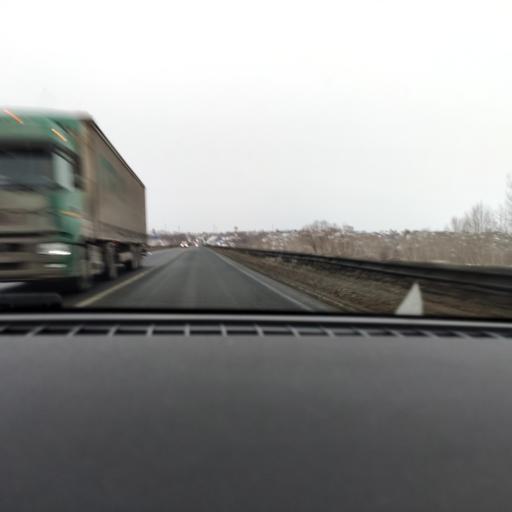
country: RU
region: Samara
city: Smyshlyayevka
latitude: 53.2302
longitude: 50.4915
